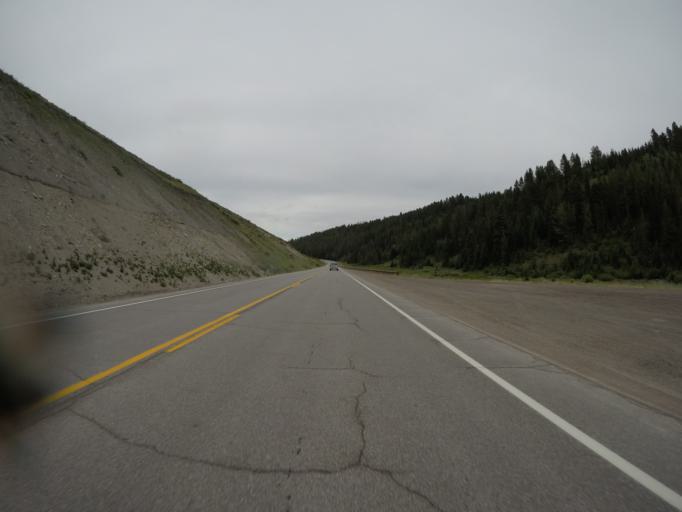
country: US
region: Wyoming
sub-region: Lincoln County
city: Afton
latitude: 42.4859
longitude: -110.9346
